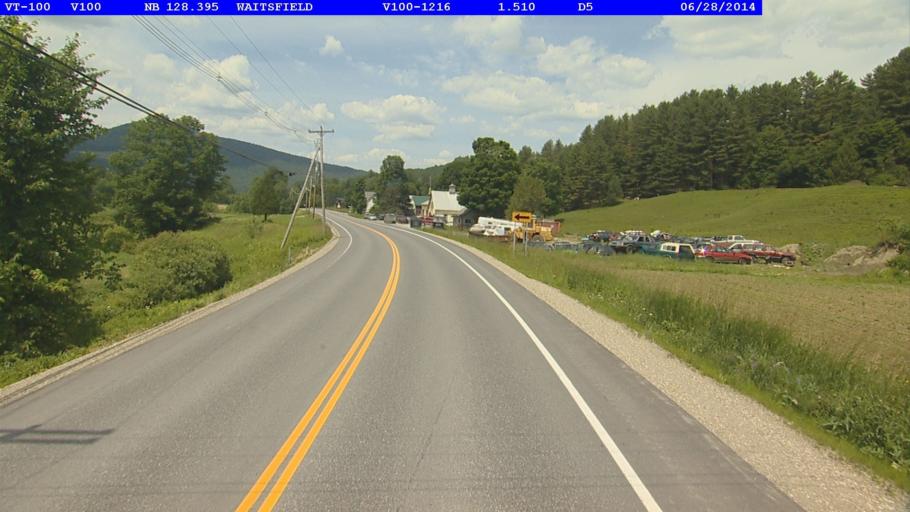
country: US
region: Vermont
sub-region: Washington County
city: Northfield
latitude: 44.1672
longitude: -72.8314
